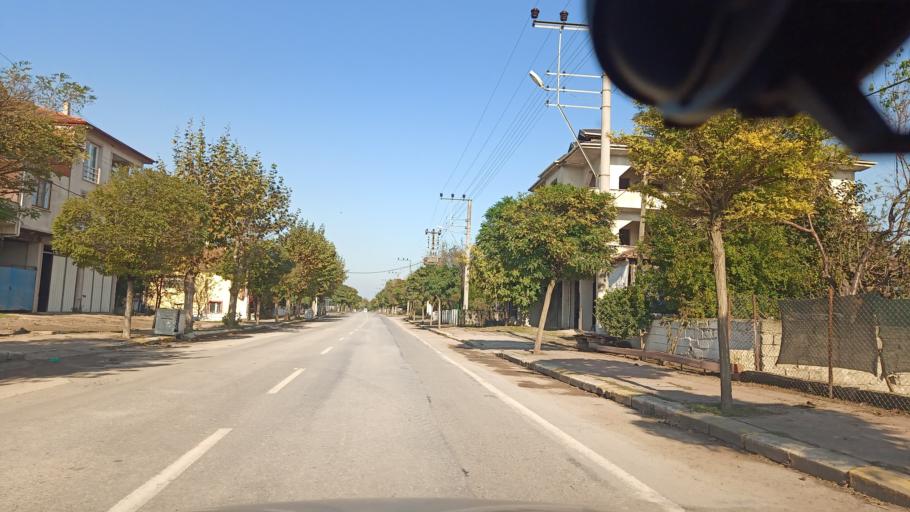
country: TR
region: Sakarya
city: Sogutlu
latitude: 40.8860
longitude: 30.4647
